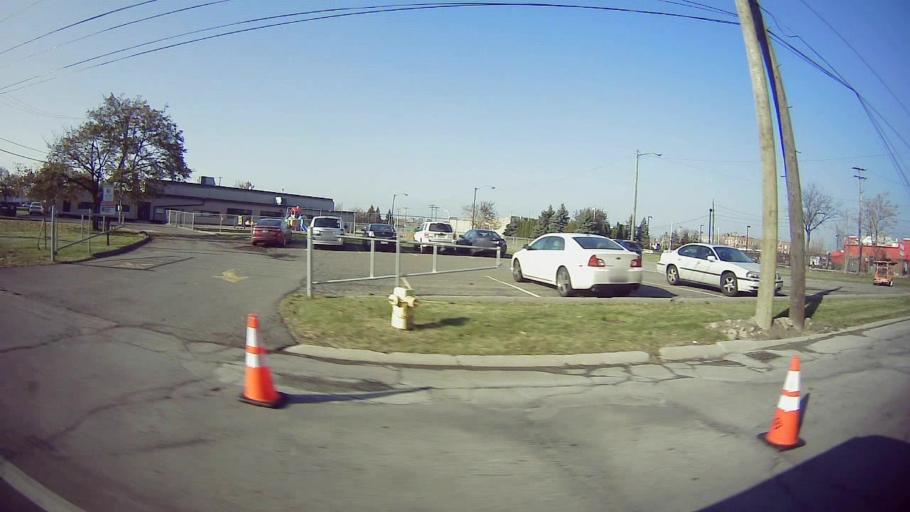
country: US
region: Michigan
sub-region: Wayne County
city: Dearborn
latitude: 42.3239
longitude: -83.1662
